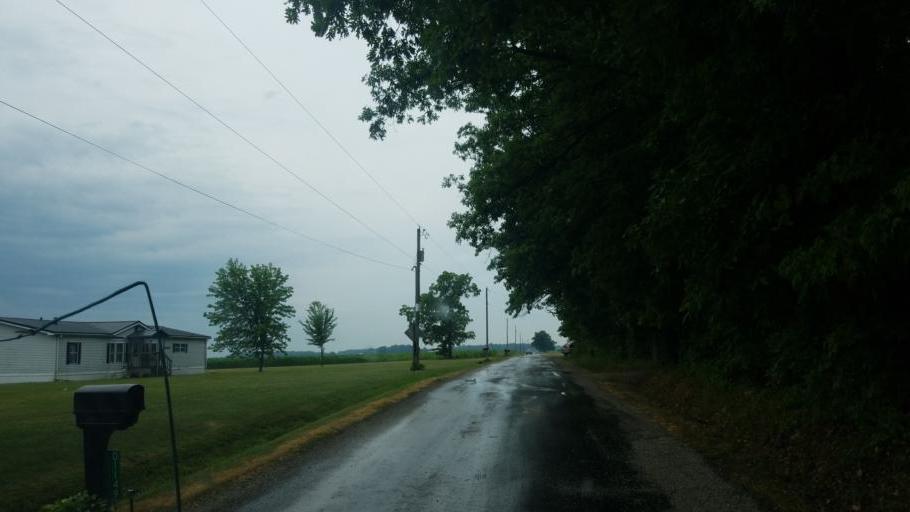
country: US
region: Ohio
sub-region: Williams County
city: Edgerton
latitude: 41.4239
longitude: -84.6704
